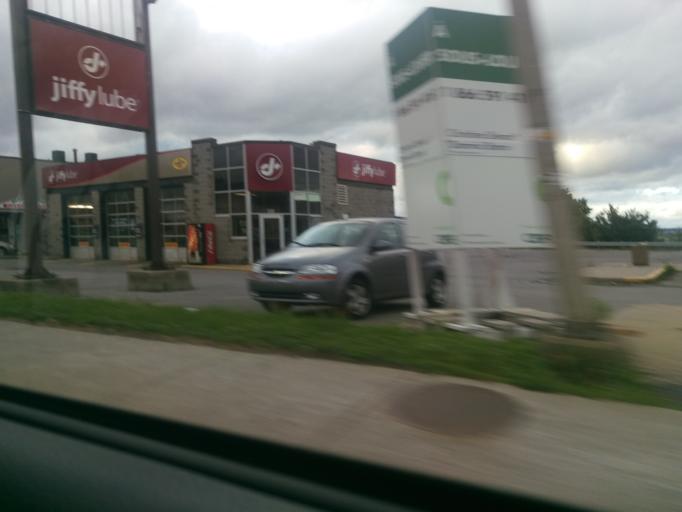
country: CA
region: Quebec
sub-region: Outaouais
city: Gatineau
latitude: 45.4524
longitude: -75.7389
